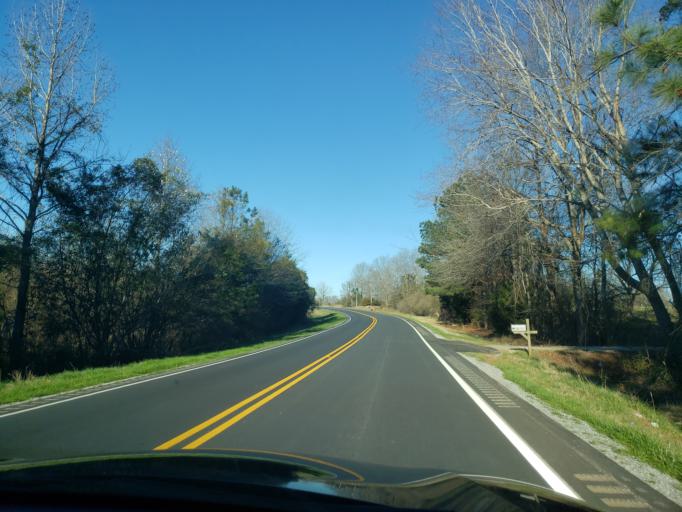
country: US
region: Alabama
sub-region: Macon County
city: Tuskegee
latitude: 32.5798
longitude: -85.7043
